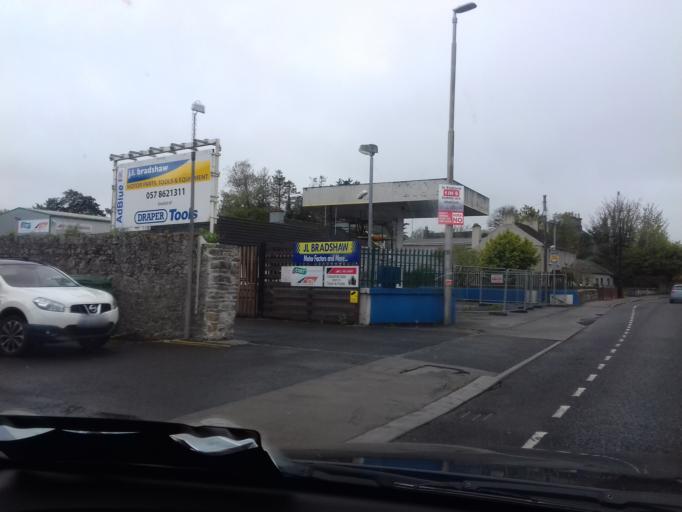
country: IE
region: Leinster
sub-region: Laois
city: Portlaoise
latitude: 53.0361
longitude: -7.2896
